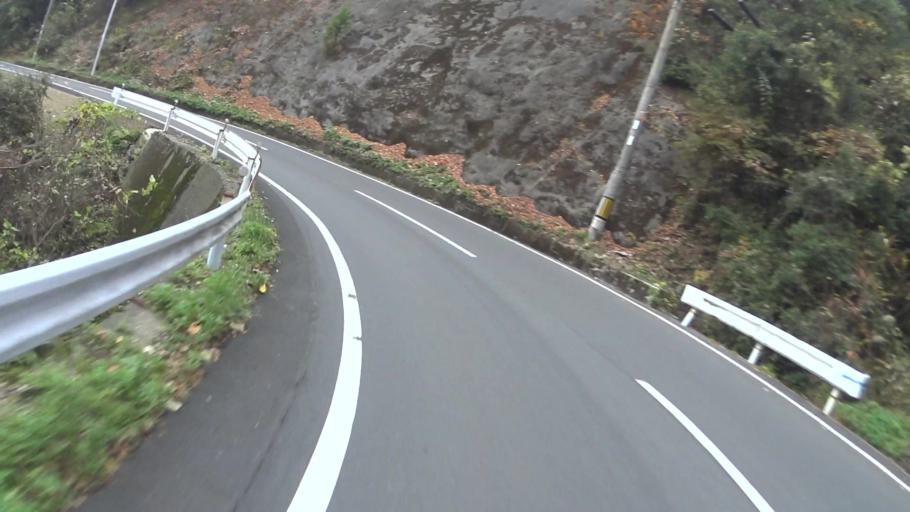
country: JP
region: Kyoto
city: Maizuru
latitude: 35.5353
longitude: 135.4432
